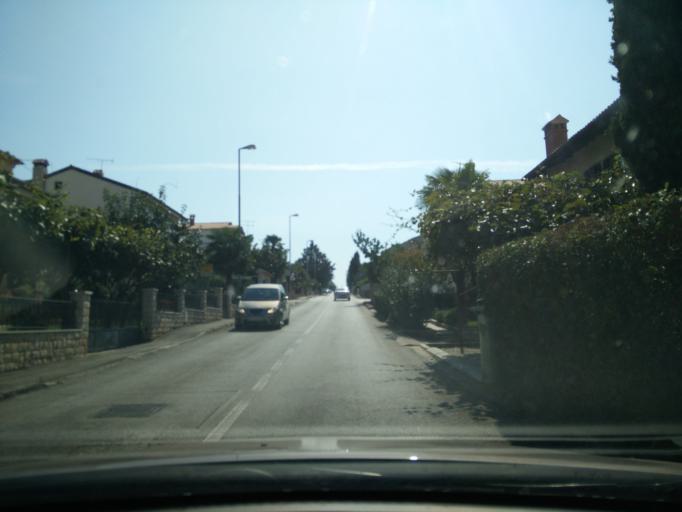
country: HR
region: Istarska
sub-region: Grad Porec
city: Porec
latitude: 45.2419
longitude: 13.6055
